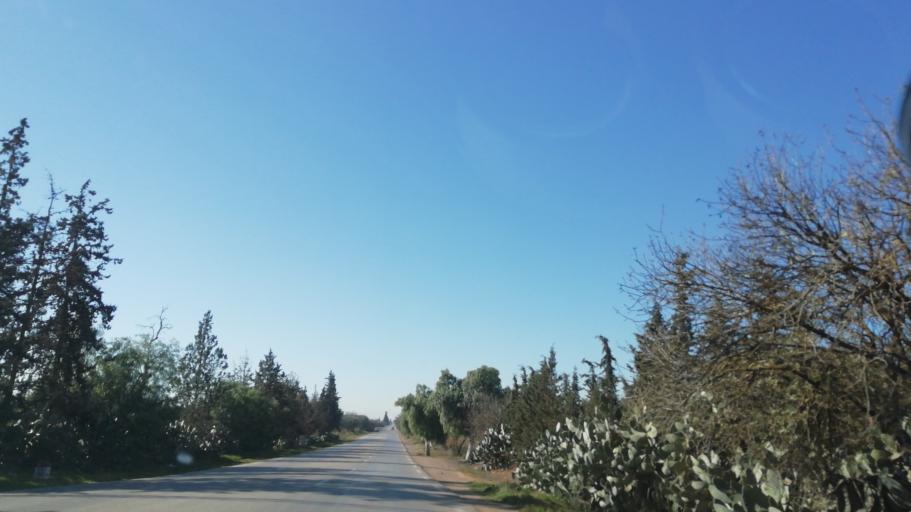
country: DZ
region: Tlemcen
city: Nedroma
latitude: 34.8355
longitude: -1.7829
